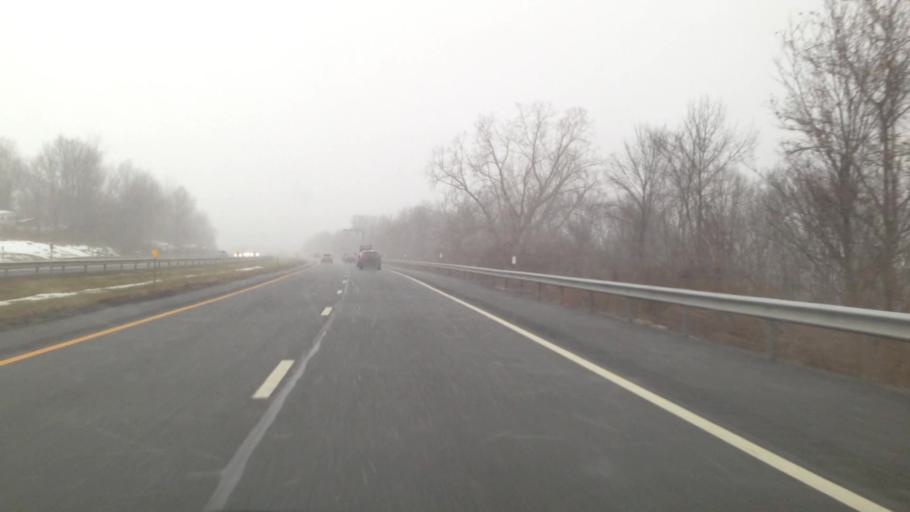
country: US
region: New York
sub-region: Montgomery County
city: Hagaman
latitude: 42.8916
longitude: -74.0861
